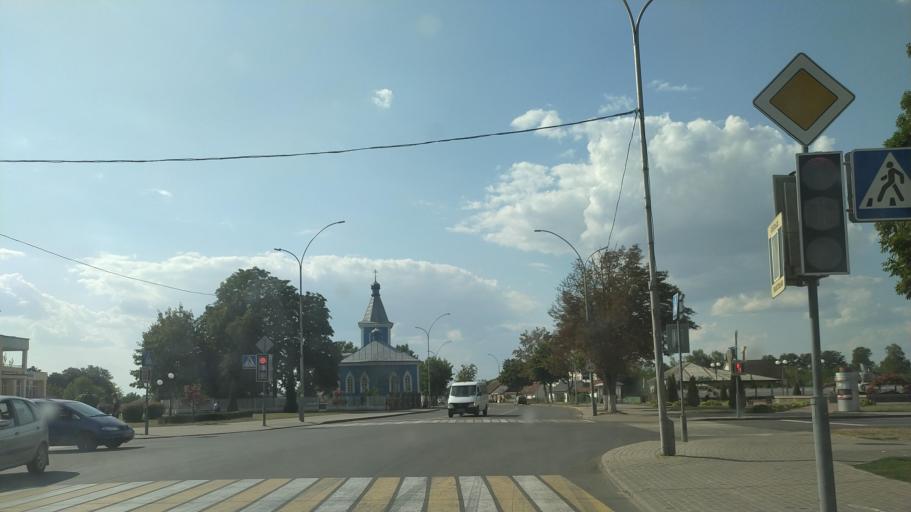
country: BY
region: Brest
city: Drahichyn
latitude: 52.1866
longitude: 25.1534
